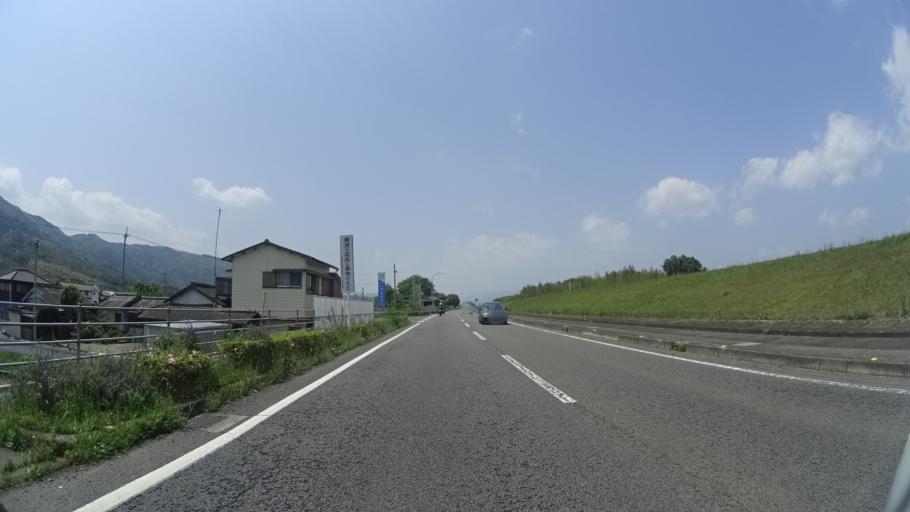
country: JP
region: Tokushima
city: Kamojimacho-jogejima
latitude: 34.0606
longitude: 134.3017
